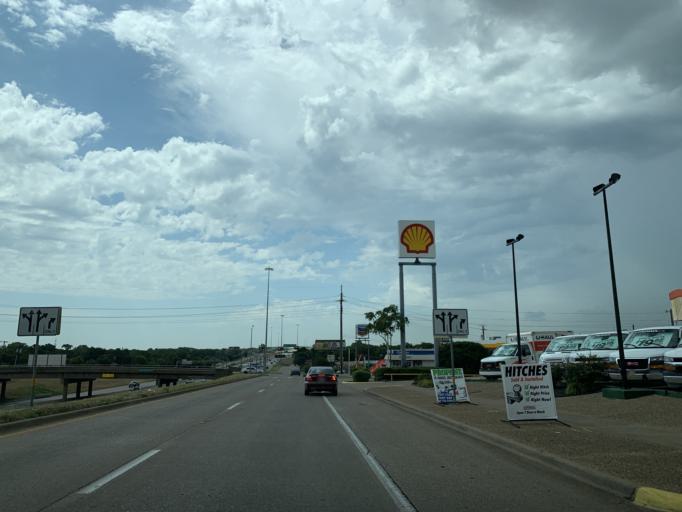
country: US
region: Texas
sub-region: Dallas County
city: DeSoto
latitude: 32.6634
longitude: -96.8235
